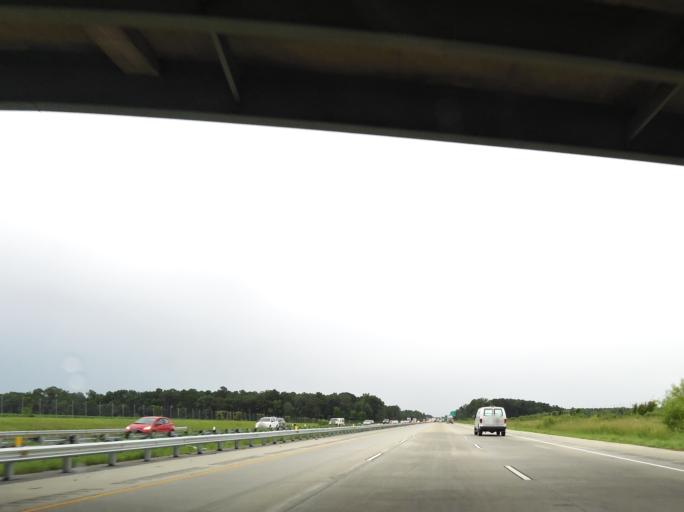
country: US
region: Georgia
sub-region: Dooly County
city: Vienna
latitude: 32.1443
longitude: -83.7575
